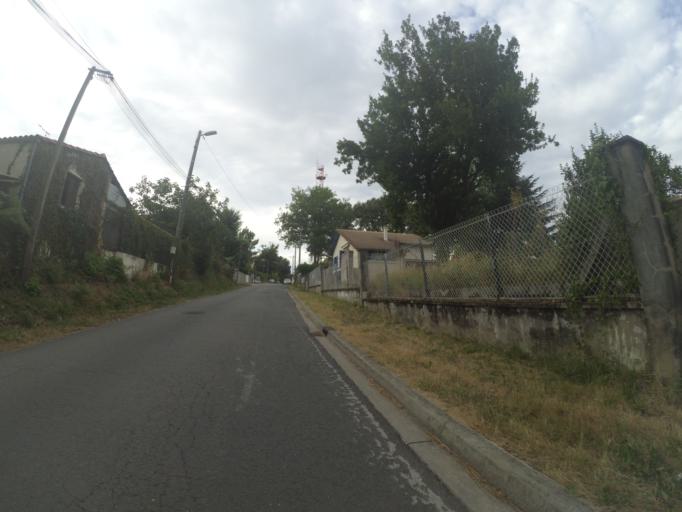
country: FR
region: Poitou-Charentes
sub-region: Departement de la Charente-Maritime
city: Meschers-sur-Gironde
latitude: 45.5661
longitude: -0.9618
